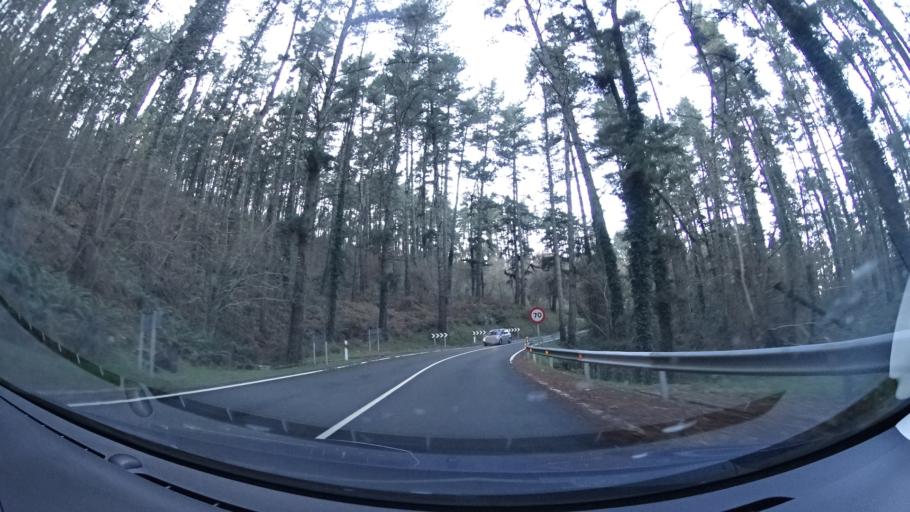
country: ES
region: Basque Country
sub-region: Bizkaia
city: Bakio
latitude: 43.3816
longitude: -2.7748
